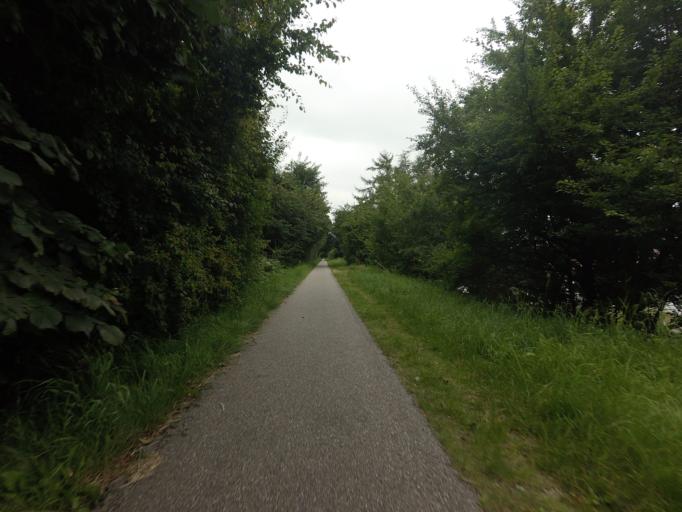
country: DK
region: Central Jutland
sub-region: Horsens Kommune
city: Braedstrup
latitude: 56.0220
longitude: 9.5247
